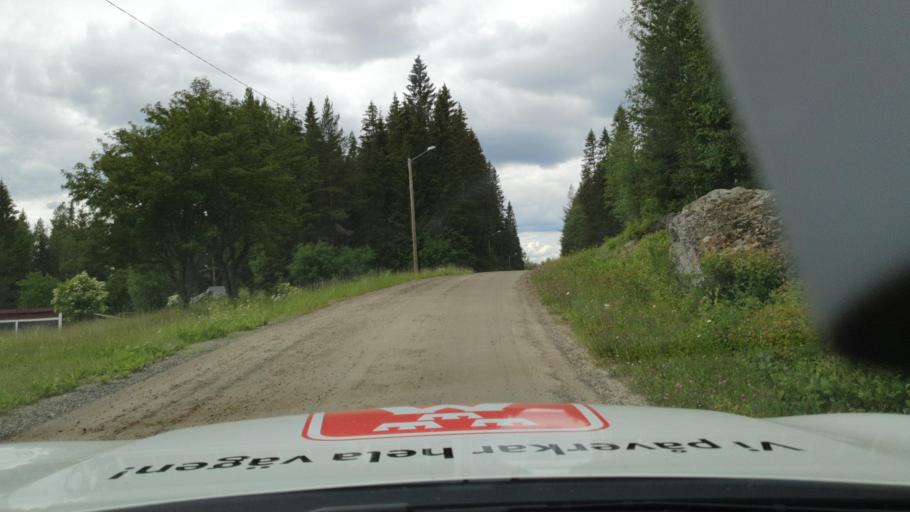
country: SE
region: Vaesterbotten
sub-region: Bjurholms Kommun
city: Bjurholm
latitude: 63.8126
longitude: 19.0406
